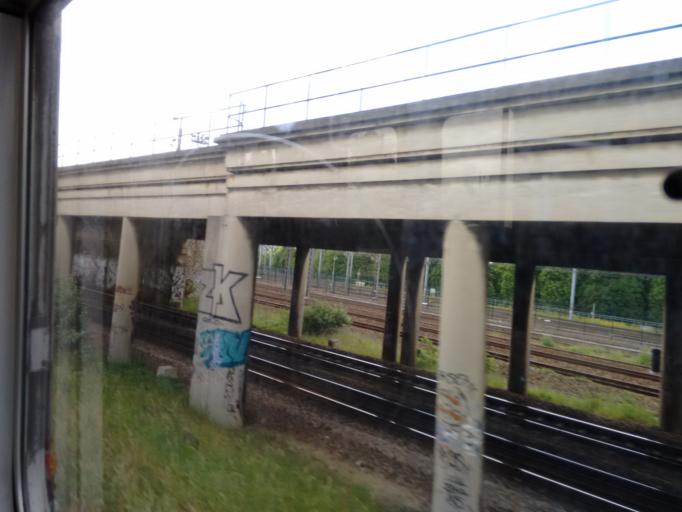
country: FR
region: Ile-de-France
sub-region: Paris
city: Saint-Ouen
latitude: 48.9094
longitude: 2.3524
